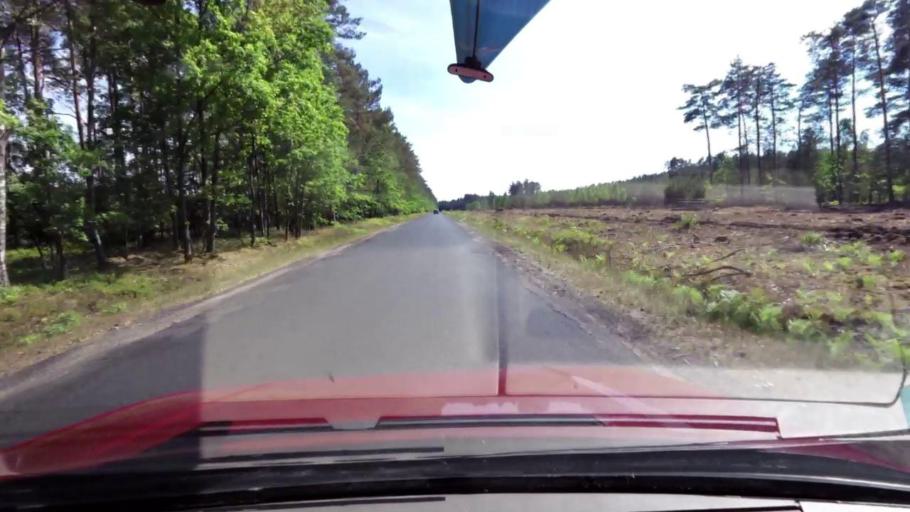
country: PL
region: Pomeranian Voivodeship
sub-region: Powiat slupski
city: Kepice
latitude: 54.3004
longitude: 16.9613
